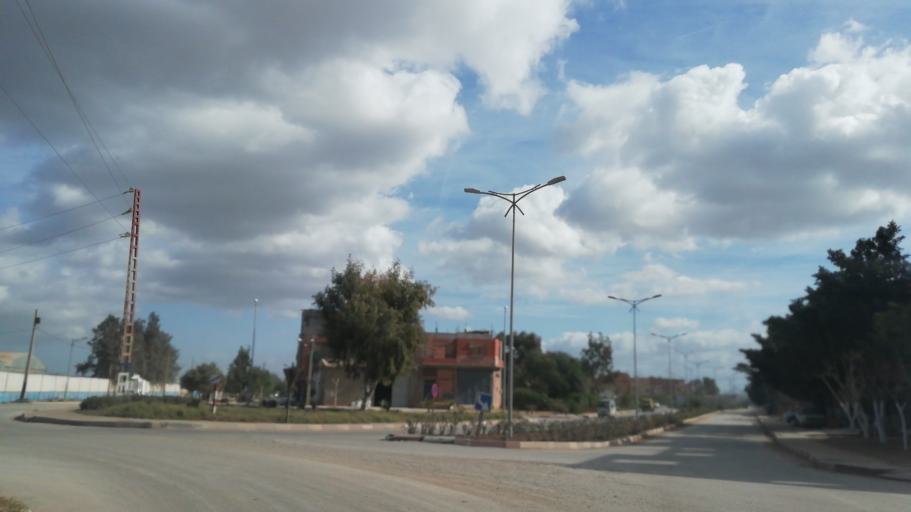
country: DZ
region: Oran
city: Es Senia
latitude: 35.6515
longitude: -0.5798
